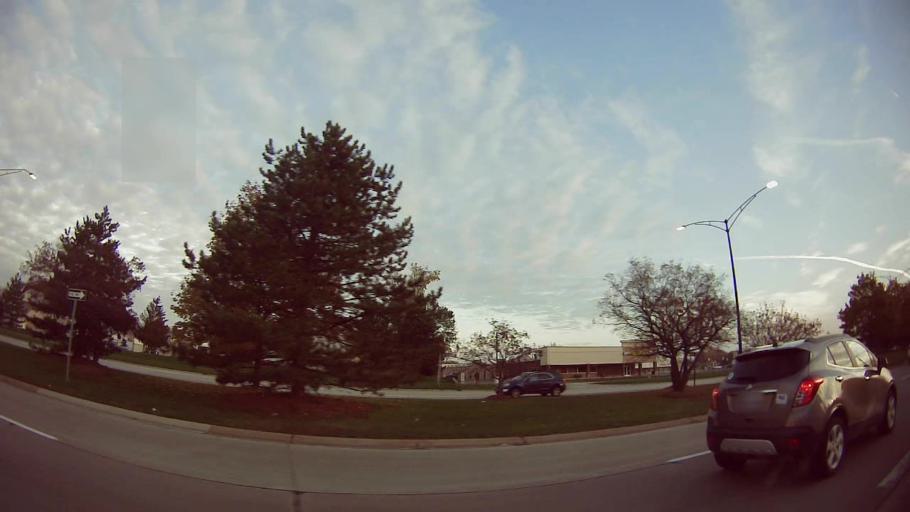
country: US
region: Michigan
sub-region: Oakland County
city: Clawson
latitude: 42.5638
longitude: -83.0915
